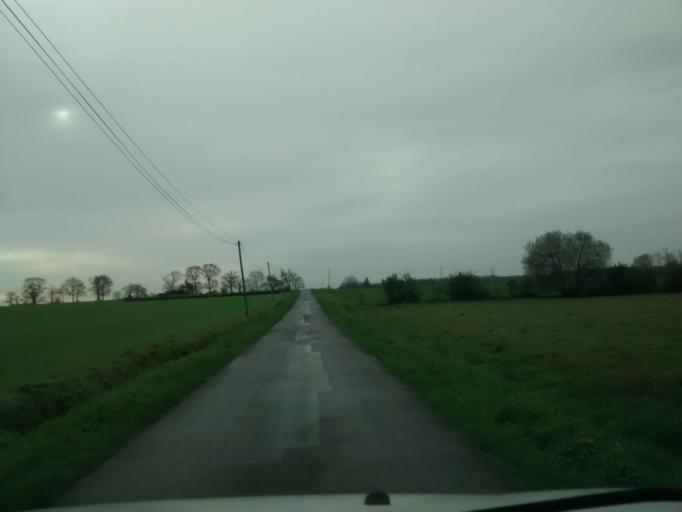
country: FR
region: Brittany
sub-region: Departement d'Ille-et-Vilaine
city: Acigne
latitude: 48.1323
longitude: -1.5541
